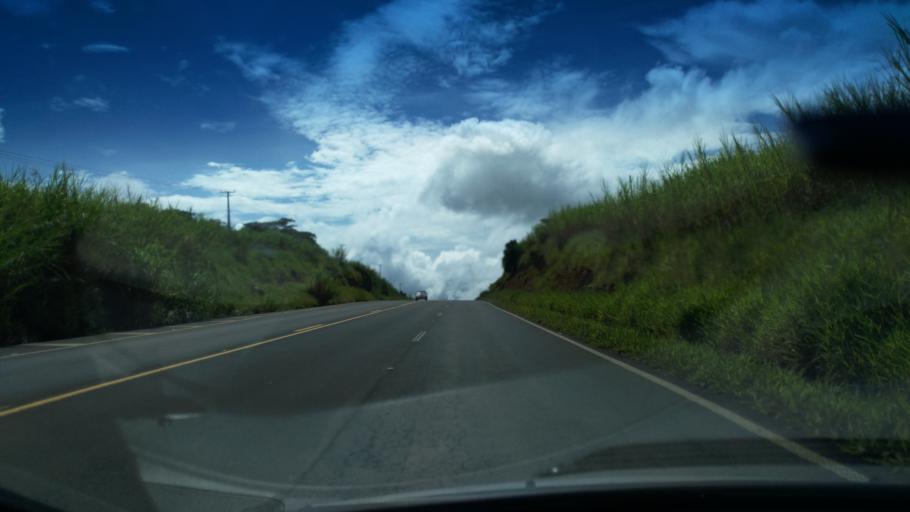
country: BR
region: Sao Paulo
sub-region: Santo Antonio Do Jardim
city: Espirito Santo do Pinhal
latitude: -22.1547
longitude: -46.7243
